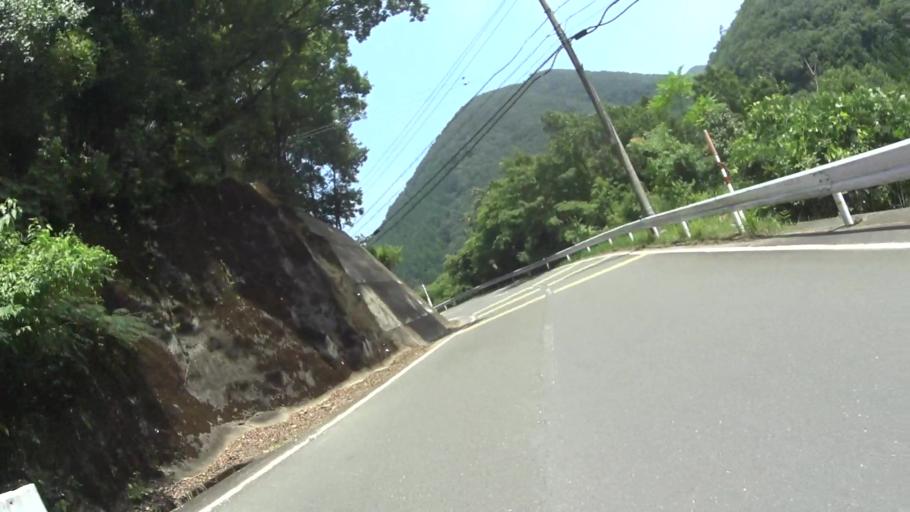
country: JP
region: Kyoto
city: Ayabe
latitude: 35.2810
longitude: 135.4300
